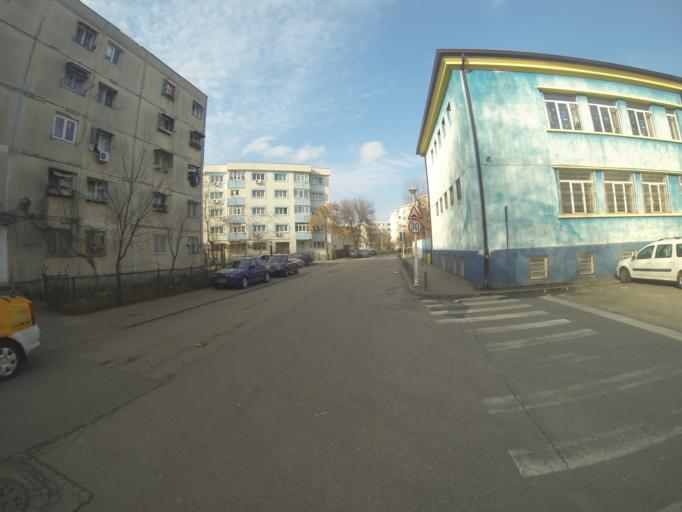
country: RO
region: Bucuresti
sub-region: Municipiul Bucuresti
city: Bucuresti
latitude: 44.4057
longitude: 26.0762
